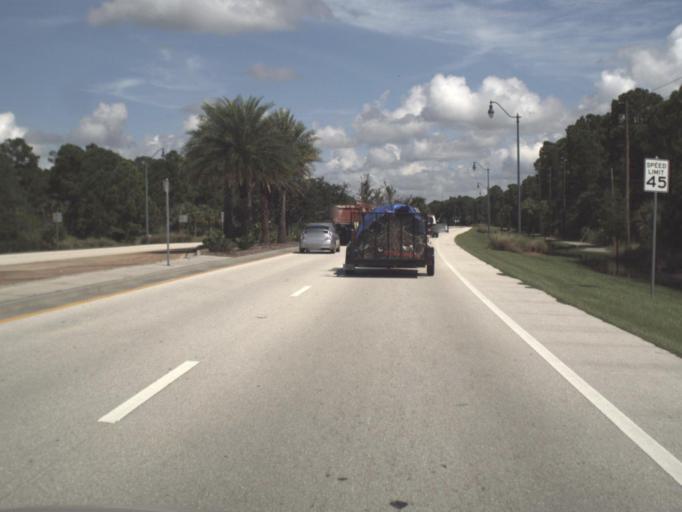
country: US
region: Florida
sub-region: Sarasota County
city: North Port
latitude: 27.0692
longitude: -82.1568
